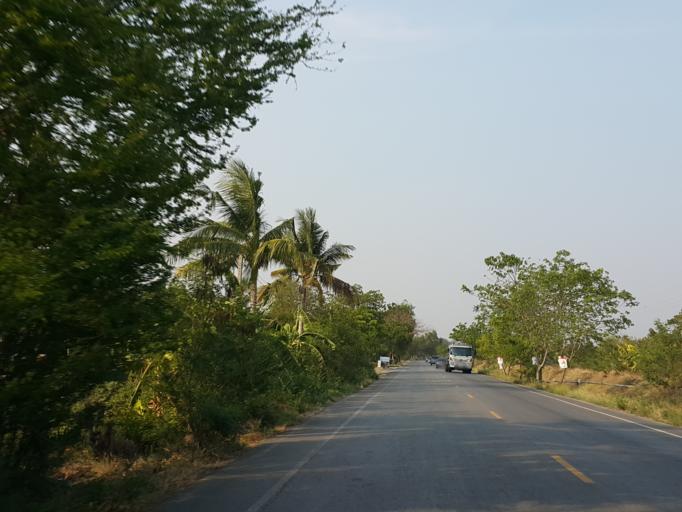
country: TH
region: Chai Nat
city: Sankhaburi
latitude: 15.0169
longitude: 100.1362
